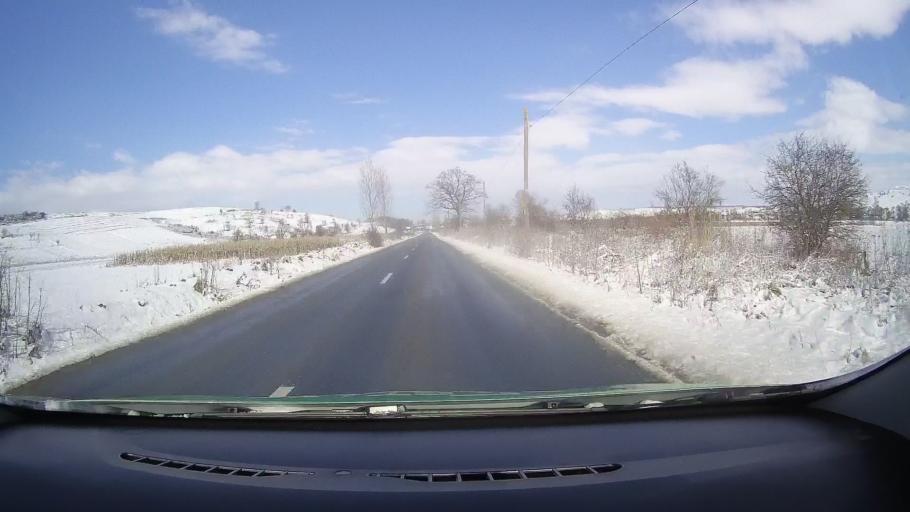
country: RO
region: Sibiu
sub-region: Comuna Nocrich
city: Nocrich
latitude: 45.8779
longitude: 24.4516
